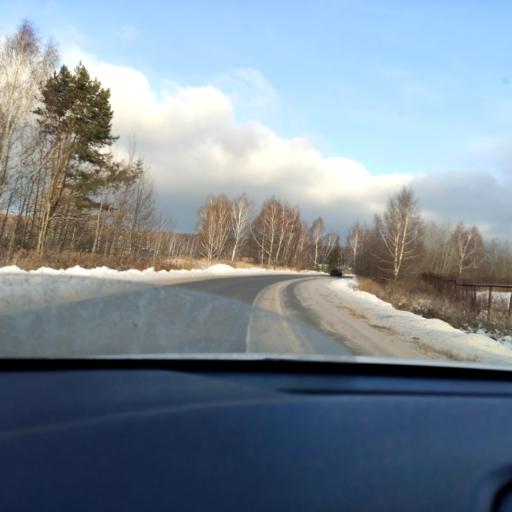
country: RU
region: Tatarstan
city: Osinovo
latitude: 55.8955
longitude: 48.8900
